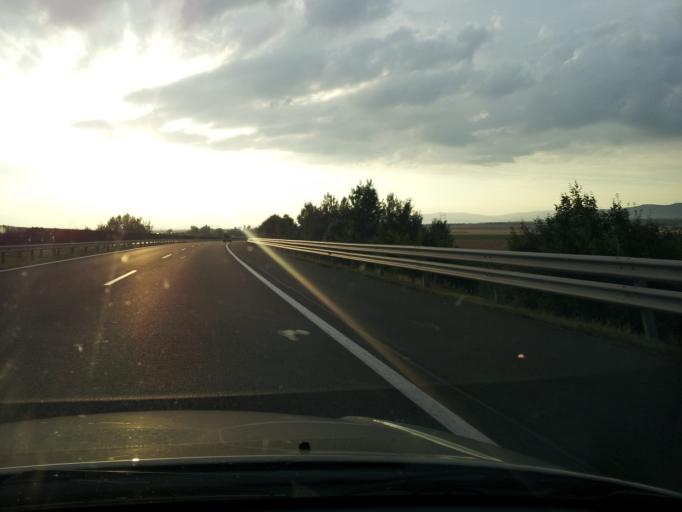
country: HU
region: Heves
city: Karacsond
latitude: 47.7089
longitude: 20.0112
